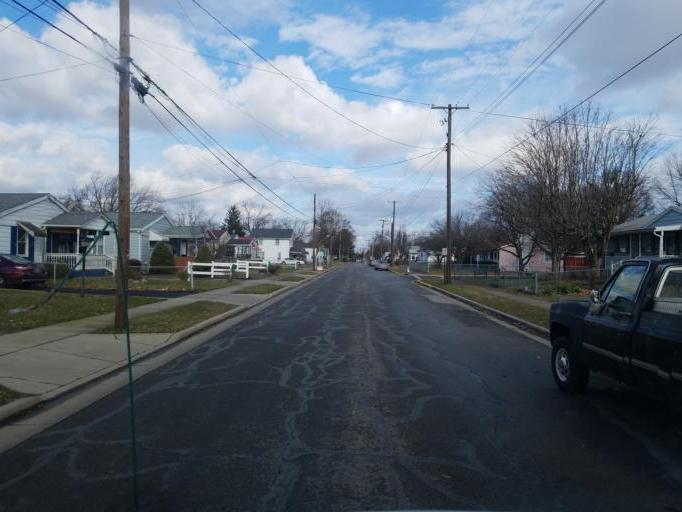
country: US
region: Ohio
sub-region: Marion County
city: Marion
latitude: 40.5814
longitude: -83.1539
